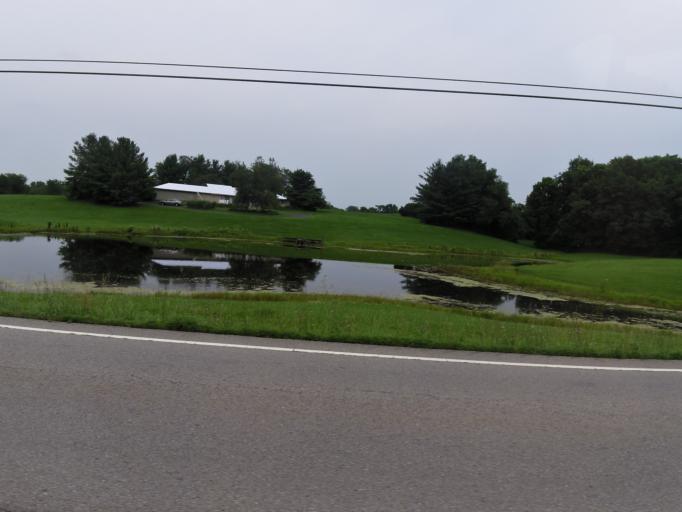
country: US
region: Ohio
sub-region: Clinton County
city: Wilmington
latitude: 39.4667
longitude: -83.8794
